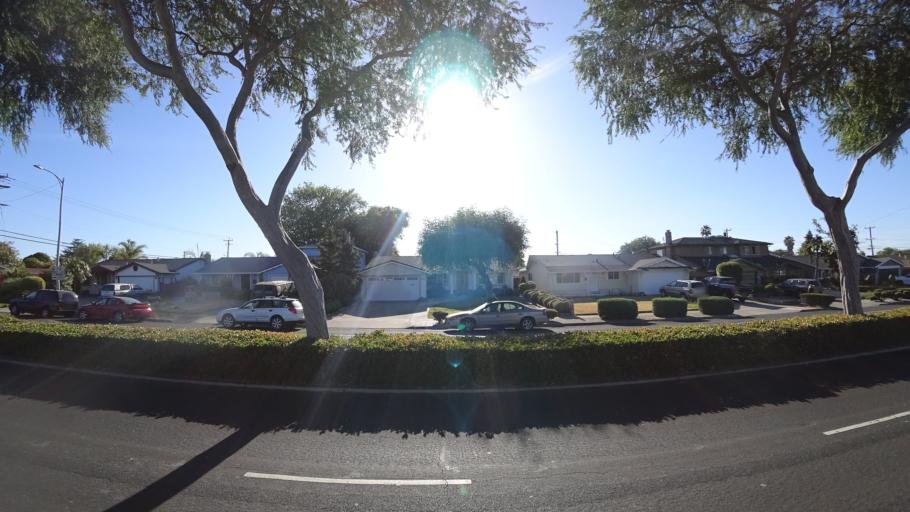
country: US
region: California
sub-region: Alameda County
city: Hayward
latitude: 37.6454
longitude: -122.0993
